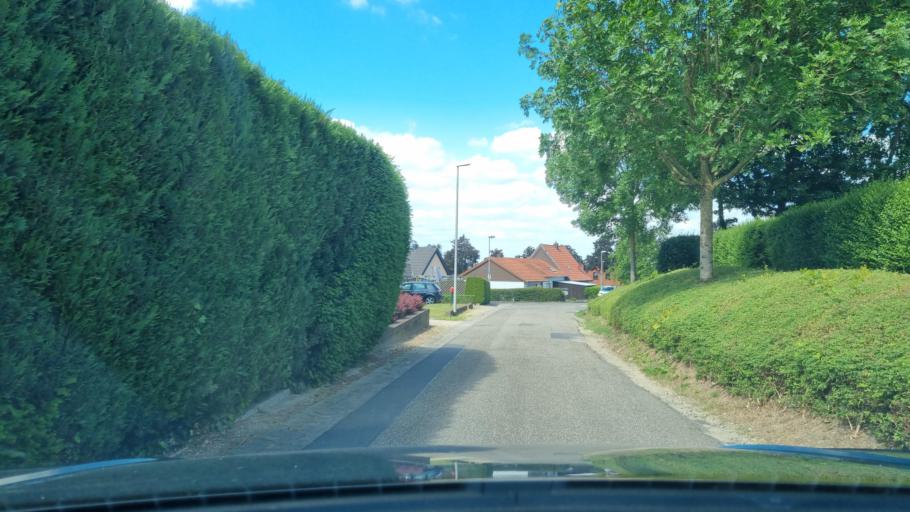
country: DE
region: North Rhine-Westphalia
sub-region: Regierungsbezirk Dusseldorf
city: Kleve
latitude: 51.7955
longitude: 6.0881
